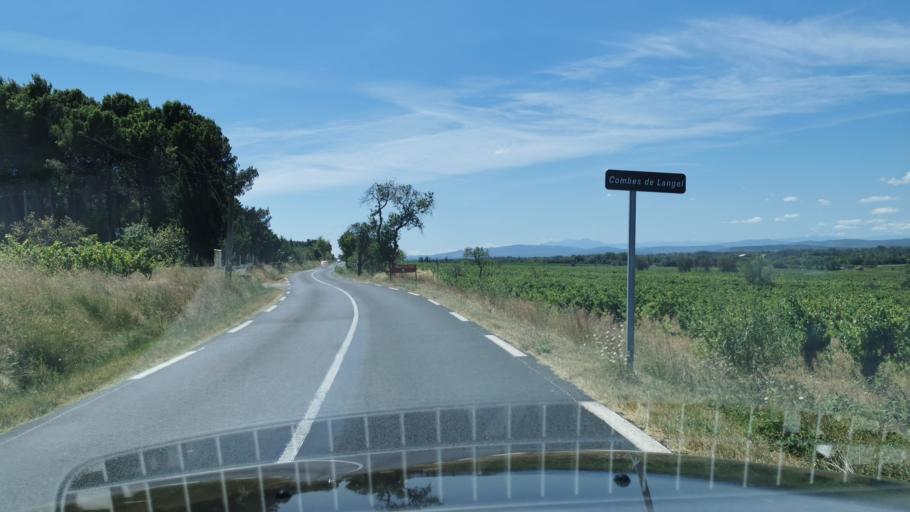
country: FR
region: Languedoc-Roussillon
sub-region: Departement de l'Aude
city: Vinassan
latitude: 43.1841
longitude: 3.0638
